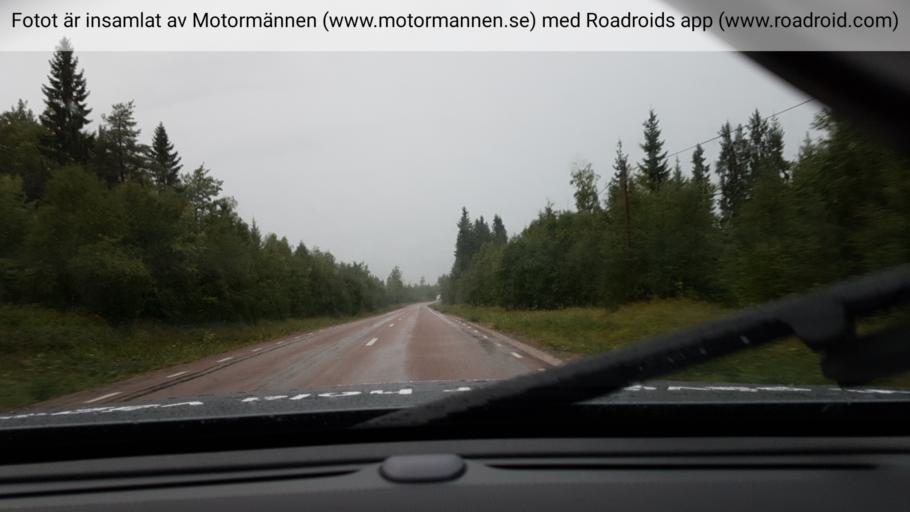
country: SE
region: Dalarna
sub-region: Rattviks Kommun
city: Raettvik
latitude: 60.8799
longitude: 15.2973
